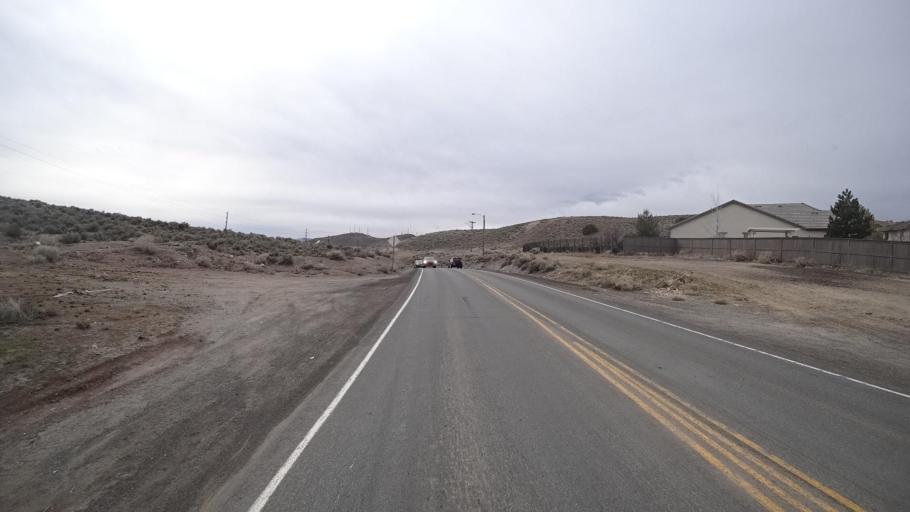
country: US
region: Nevada
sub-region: Washoe County
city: Golden Valley
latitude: 39.6031
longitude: -119.8090
